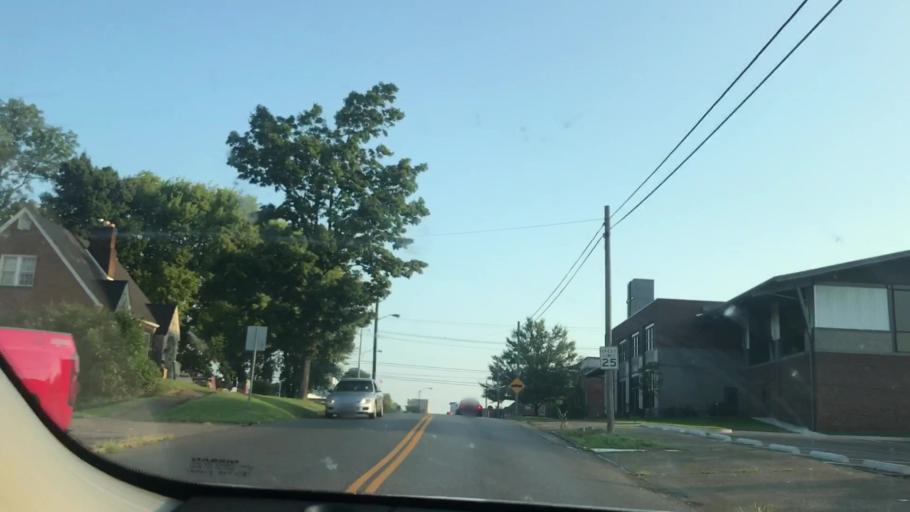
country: US
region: Kentucky
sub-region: Calloway County
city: Murray
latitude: 36.6076
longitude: -88.3021
